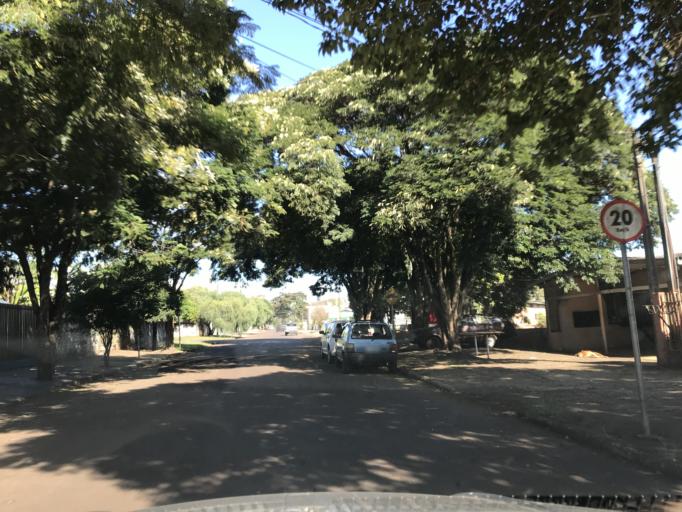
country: BR
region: Parana
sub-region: Cascavel
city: Cascavel
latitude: -24.9408
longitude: -53.4684
